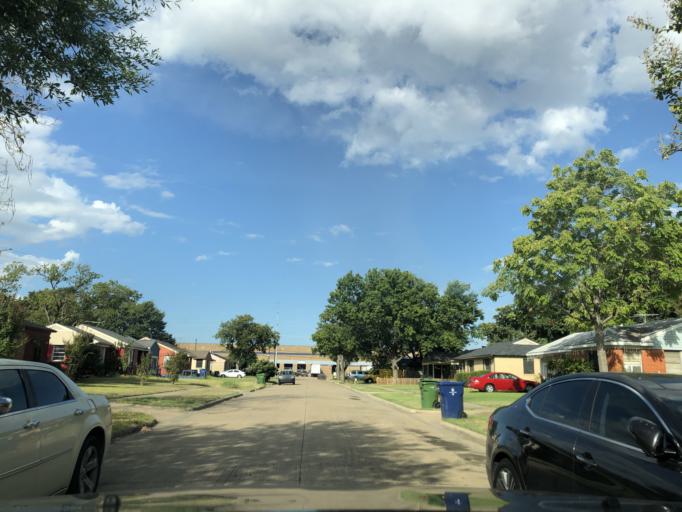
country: US
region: Texas
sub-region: Dallas County
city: Garland
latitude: 32.8825
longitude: -96.6636
